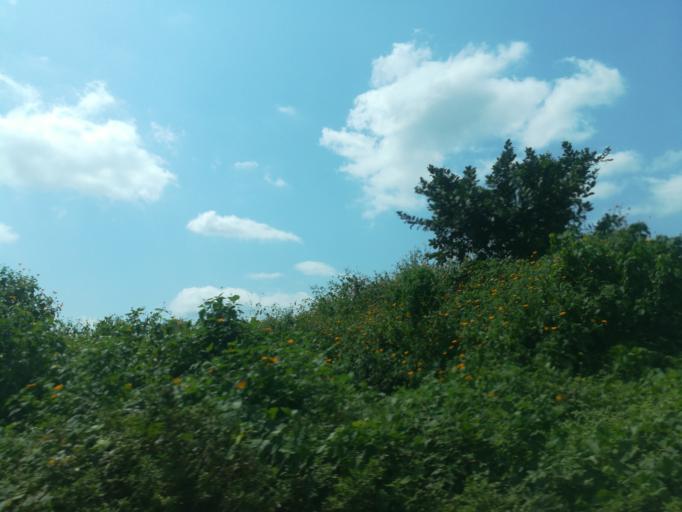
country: NG
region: Oyo
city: Moniya
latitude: 7.5467
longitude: 3.9106
